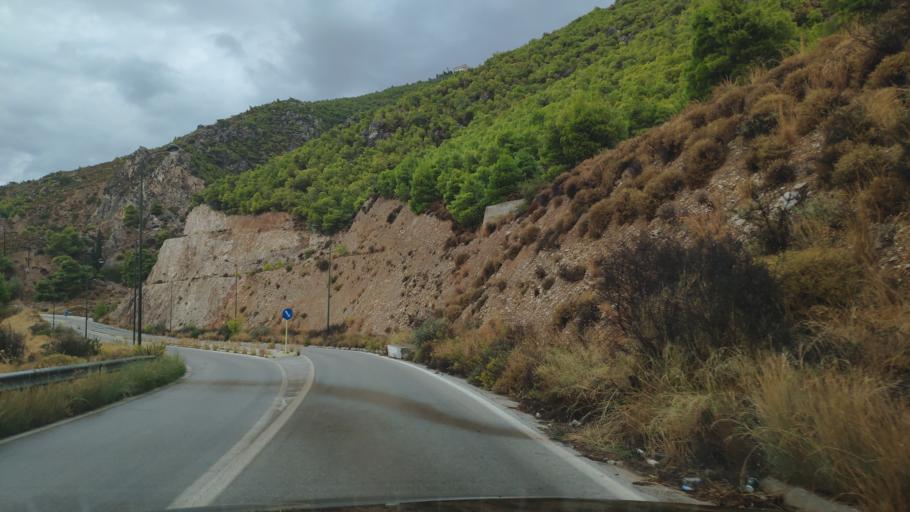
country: GR
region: Peloponnese
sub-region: Nomos Korinthias
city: Loutraki
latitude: 37.9819
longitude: 22.9792
